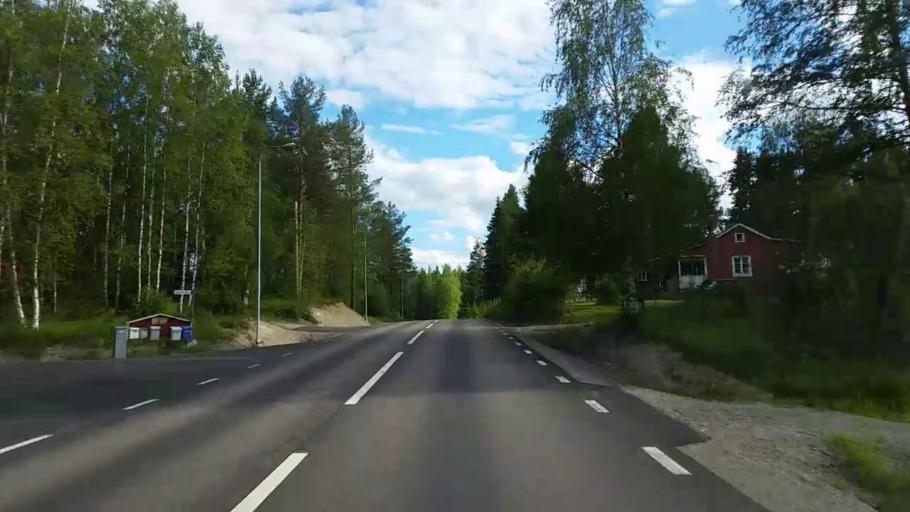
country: SE
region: Gaevleborg
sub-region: Ljusdals Kommun
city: Farila
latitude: 61.9262
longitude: 15.8735
